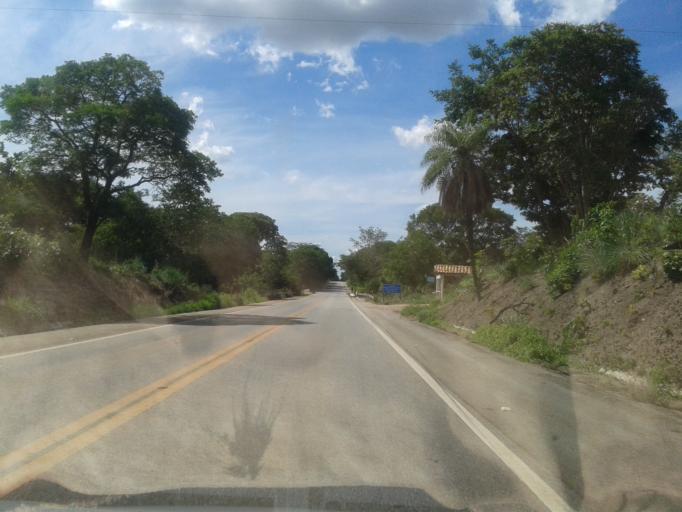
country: BR
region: Goias
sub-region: Itapuranga
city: Itapuranga
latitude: -15.4843
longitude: -50.3283
